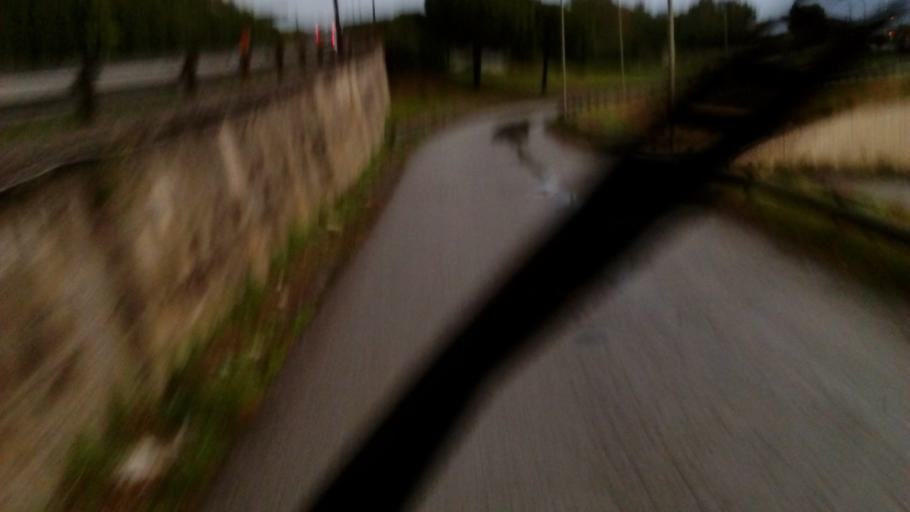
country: IT
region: Sicily
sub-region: Messina
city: Larderia
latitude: 38.1319
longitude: 15.5198
